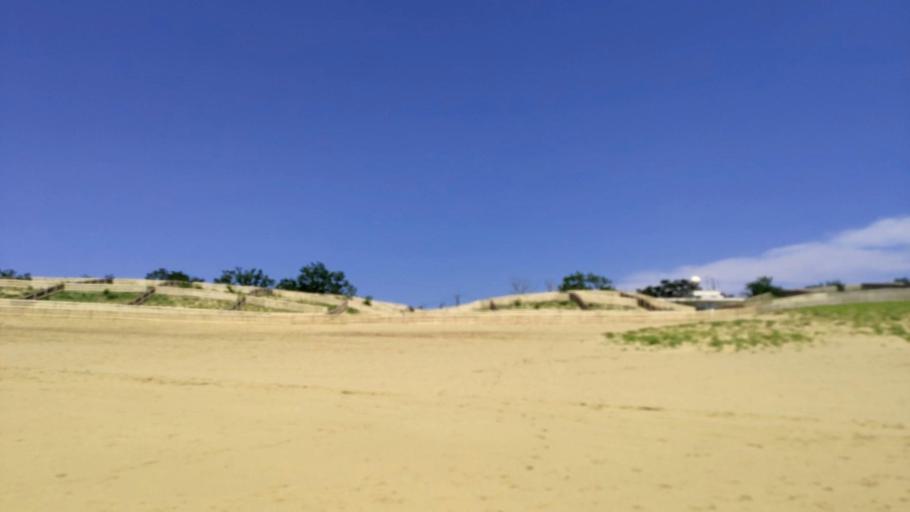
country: JP
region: Tottori
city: Tottori
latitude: 35.5420
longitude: 134.2350
